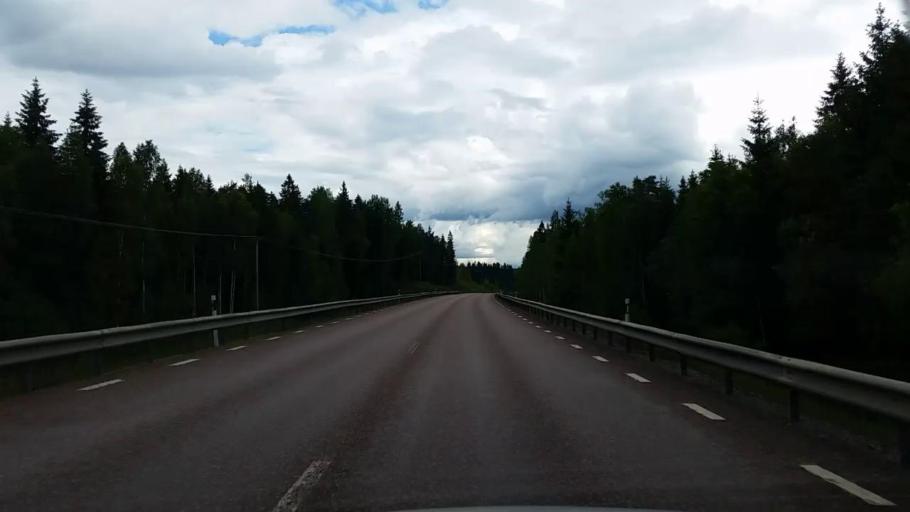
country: SE
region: Gaevleborg
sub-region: Hofors Kommun
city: Hofors
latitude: 60.5080
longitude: 16.4330
